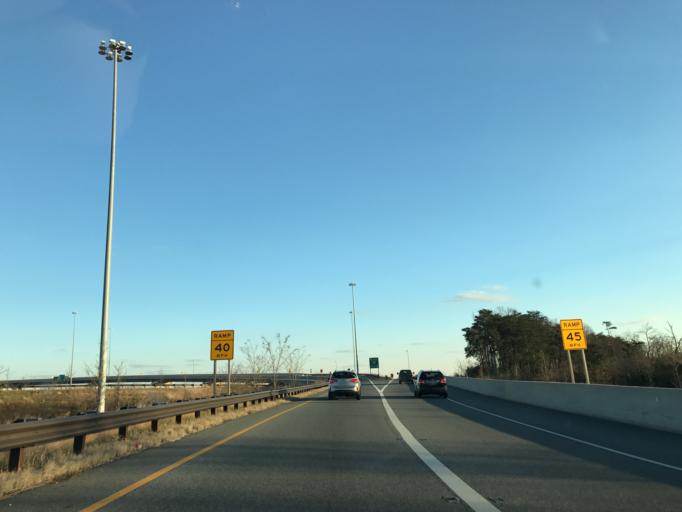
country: US
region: Maryland
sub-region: Prince George's County
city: West Laurel
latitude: 39.0741
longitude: -76.9095
